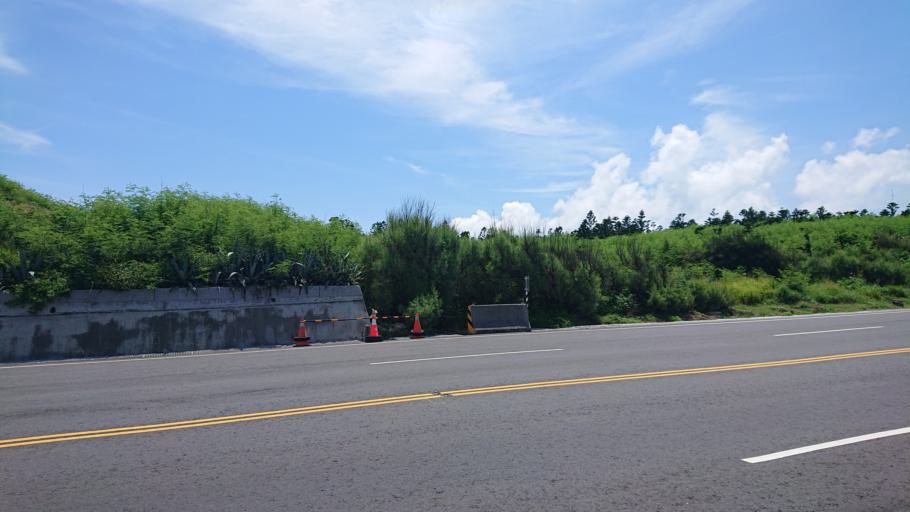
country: TW
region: Taiwan
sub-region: Penghu
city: Ma-kung
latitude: 23.6266
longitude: 119.6036
